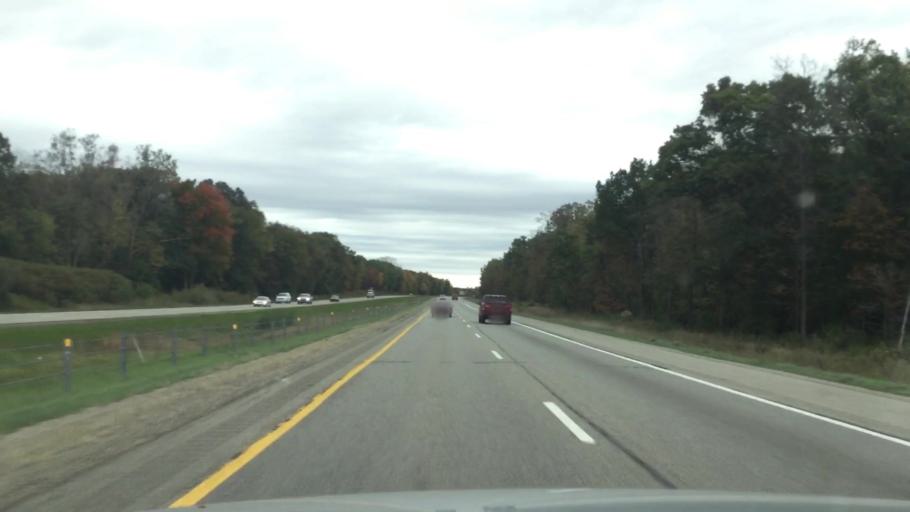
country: US
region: Michigan
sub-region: Livingston County
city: Brighton
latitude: 42.5646
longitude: -83.7403
